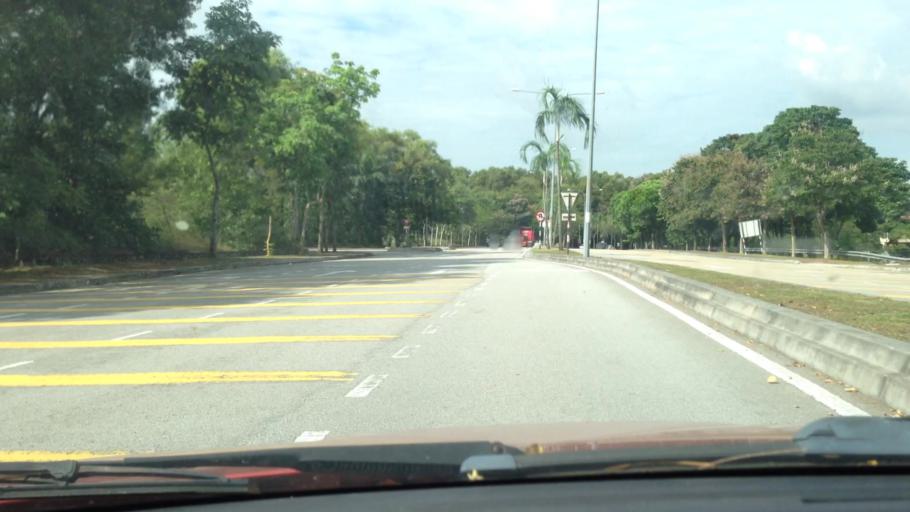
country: MY
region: Selangor
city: Subang Jaya
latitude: 3.0509
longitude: 101.5704
